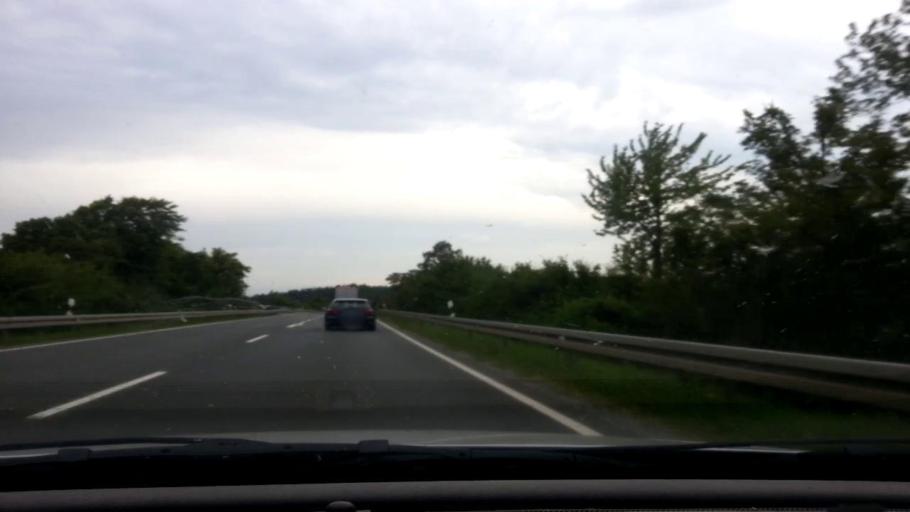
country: DE
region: Bavaria
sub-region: Upper Franconia
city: Seybothenreuth
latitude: 49.9000
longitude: 11.6979
